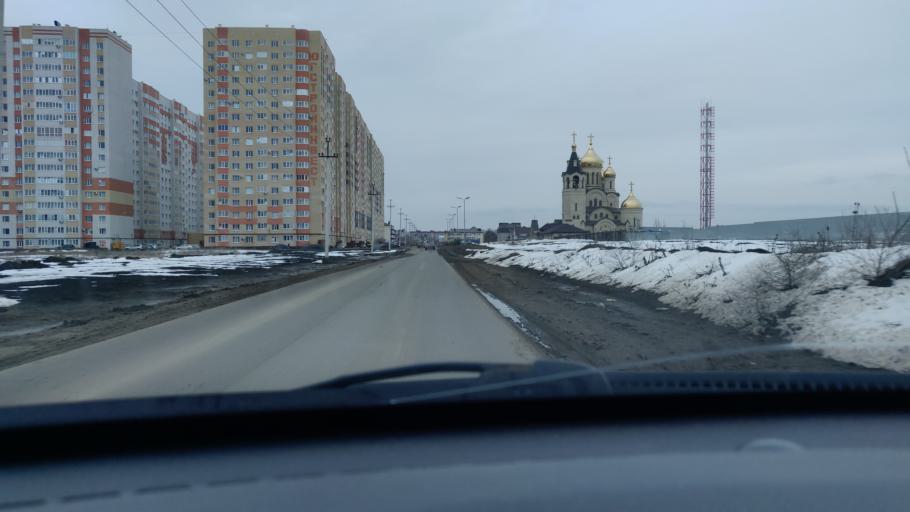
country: RU
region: Stavropol'skiy
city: Tatarka
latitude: 45.0103
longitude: 41.8984
